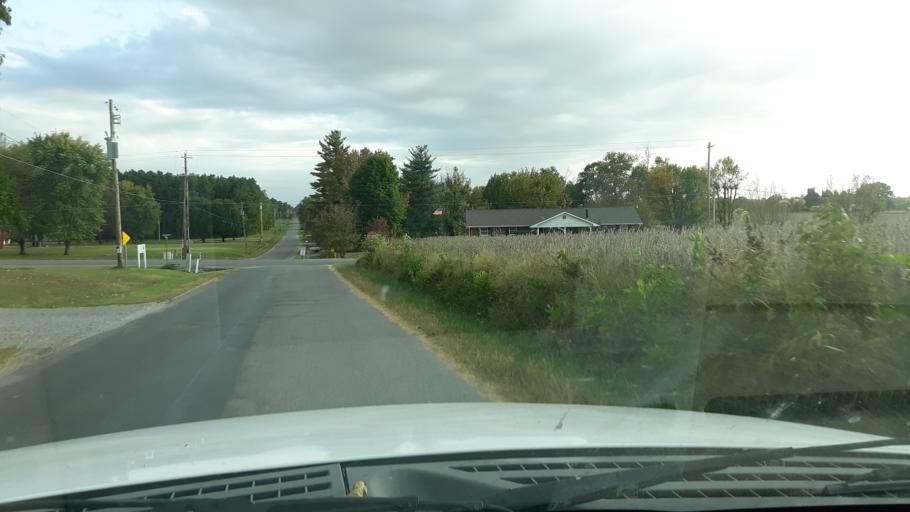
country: US
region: Illinois
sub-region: Saline County
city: Eldorado
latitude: 37.8245
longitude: -88.5025
